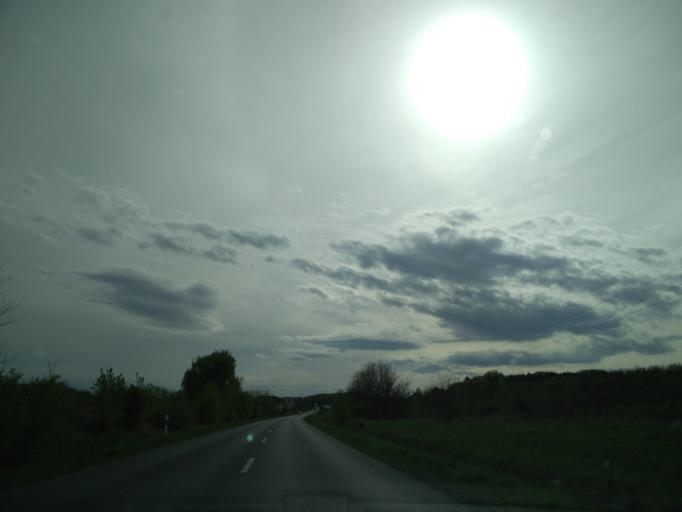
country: HU
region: Zala
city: Zalaegerszeg
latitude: 46.8675
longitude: 16.8537
